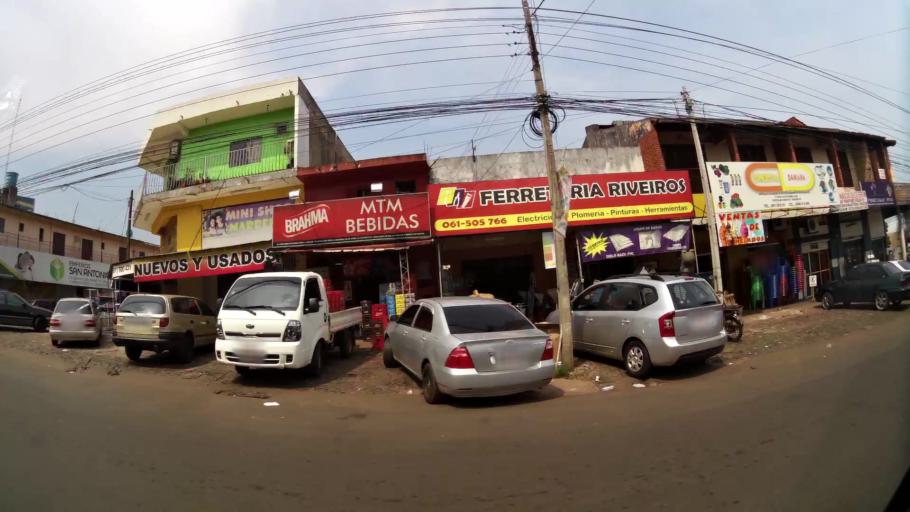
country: PY
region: Alto Parana
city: Presidente Franco
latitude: -25.5351
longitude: -54.6100
